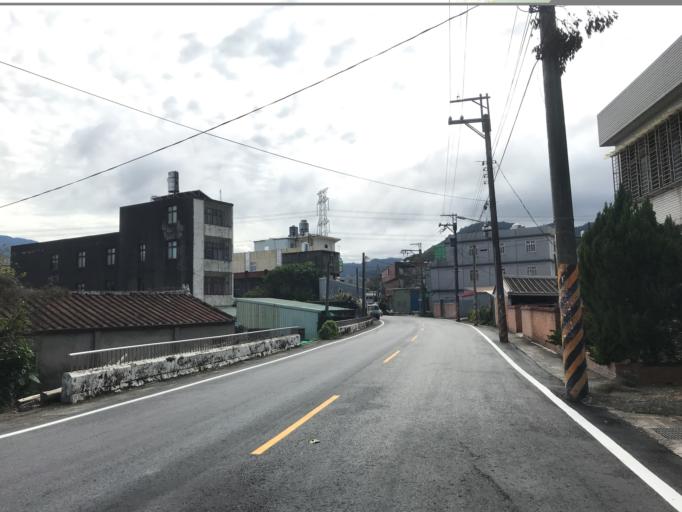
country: TW
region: Taiwan
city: Daxi
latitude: 24.8331
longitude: 121.2441
